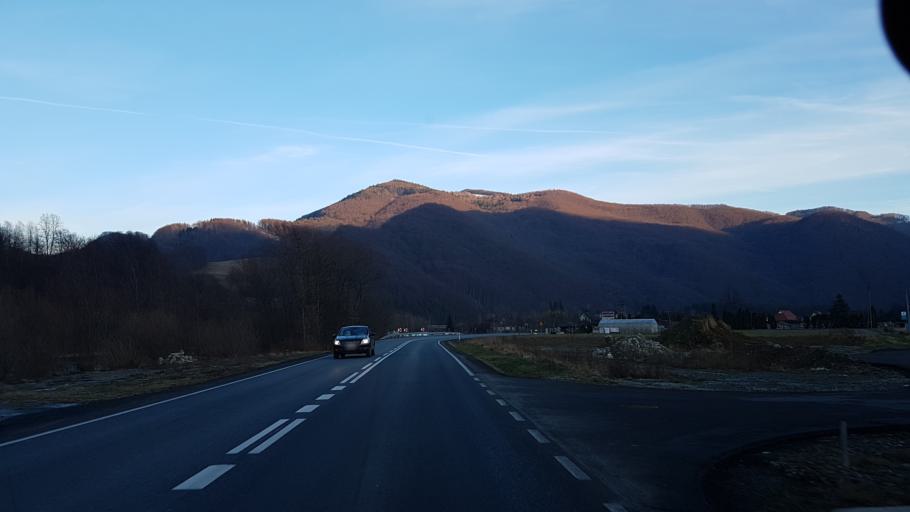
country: PL
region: Lesser Poland Voivodeship
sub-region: Powiat nowosadecki
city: Rytro
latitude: 49.5000
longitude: 20.6704
